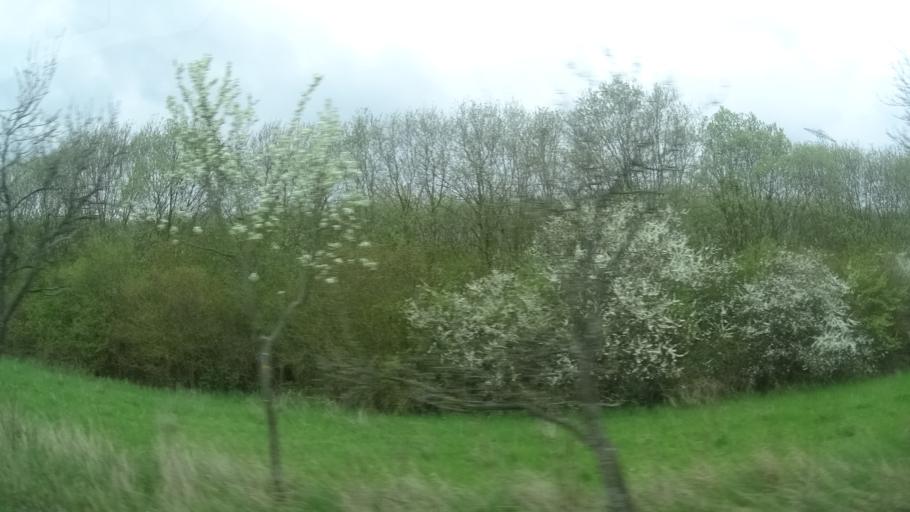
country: DE
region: Thuringia
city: Behringen
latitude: 50.7761
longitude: 11.0111
